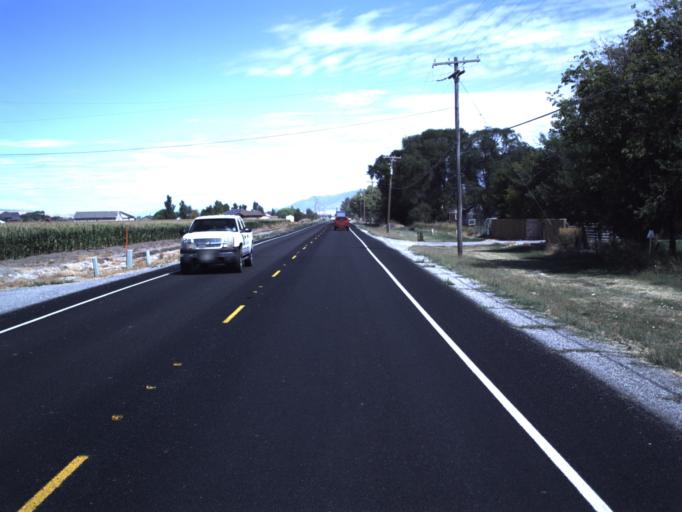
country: US
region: Utah
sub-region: Box Elder County
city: Garland
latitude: 41.7311
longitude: -112.1431
